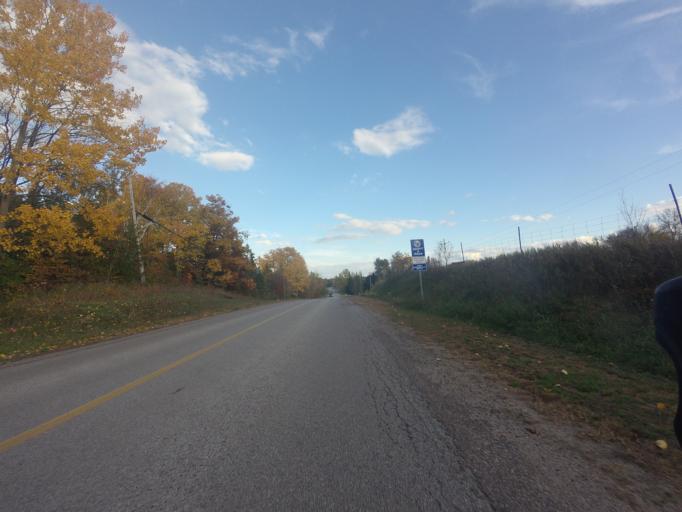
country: CA
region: Ontario
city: Pembroke
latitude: 45.5249
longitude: -77.0817
